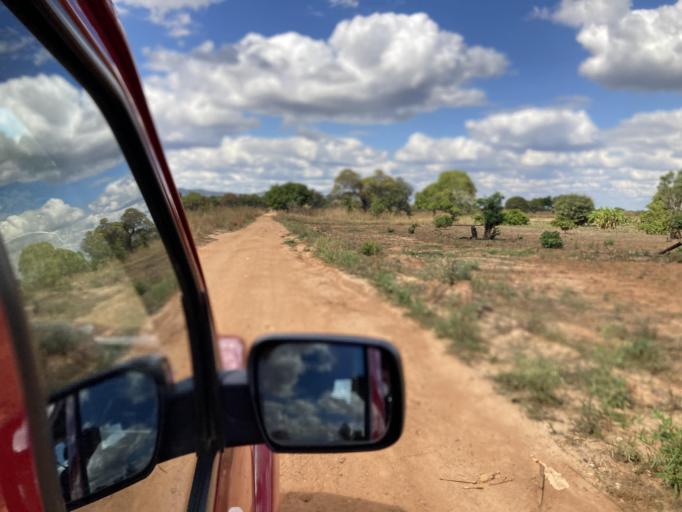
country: MZ
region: Cabo Delgado
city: Montepuez
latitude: -13.1262
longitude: 39.0399
